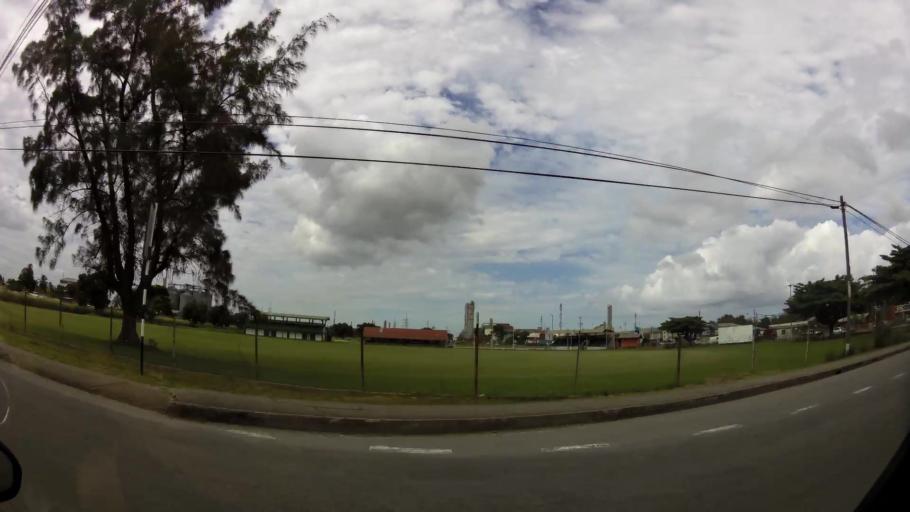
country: TT
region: Couva-Tabaquite-Talparo
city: Couva
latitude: 10.4138
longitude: -61.4710
